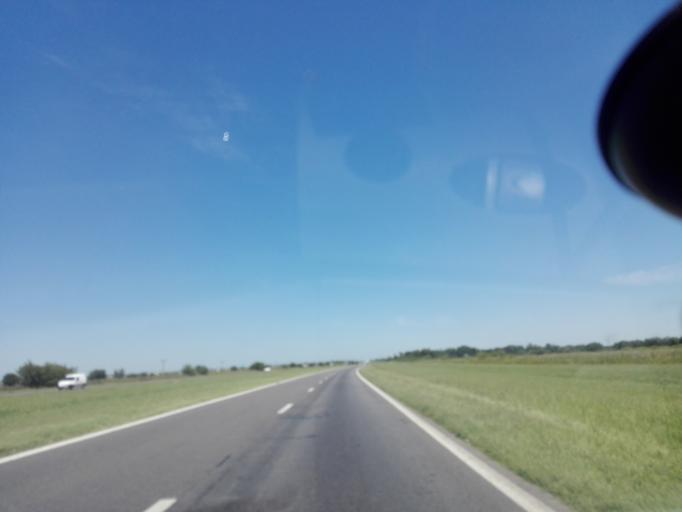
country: AR
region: Santa Fe
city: Funes
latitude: -32.9334
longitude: -60.8547
